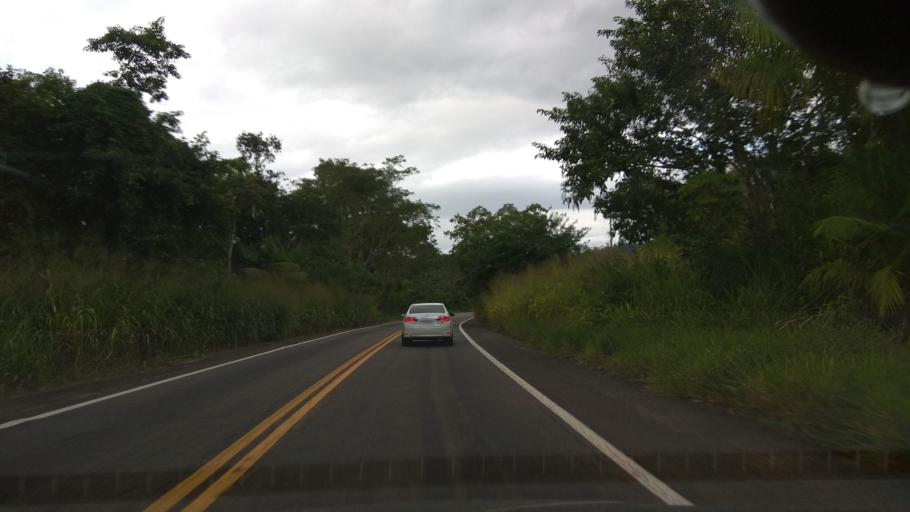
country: BR
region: Bahia
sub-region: Ubata
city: Ubata
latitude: -14.2293
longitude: -39.4494
